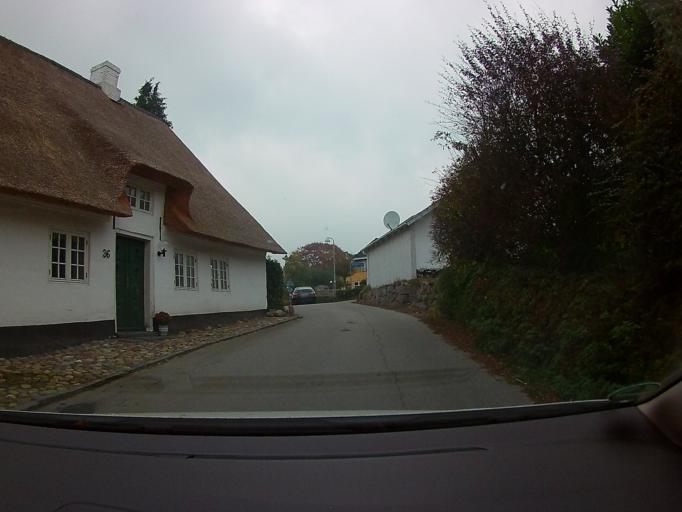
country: DE
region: Schleswig-Holstein
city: Wees
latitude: 54.8602
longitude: 9.4961
